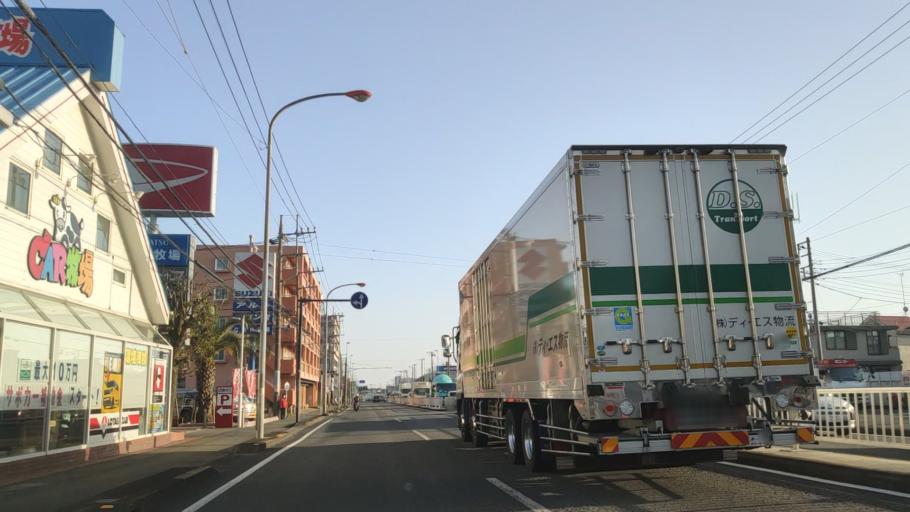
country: JP
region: Kanagawa
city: Zama
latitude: 35.4817
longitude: 139.3658
